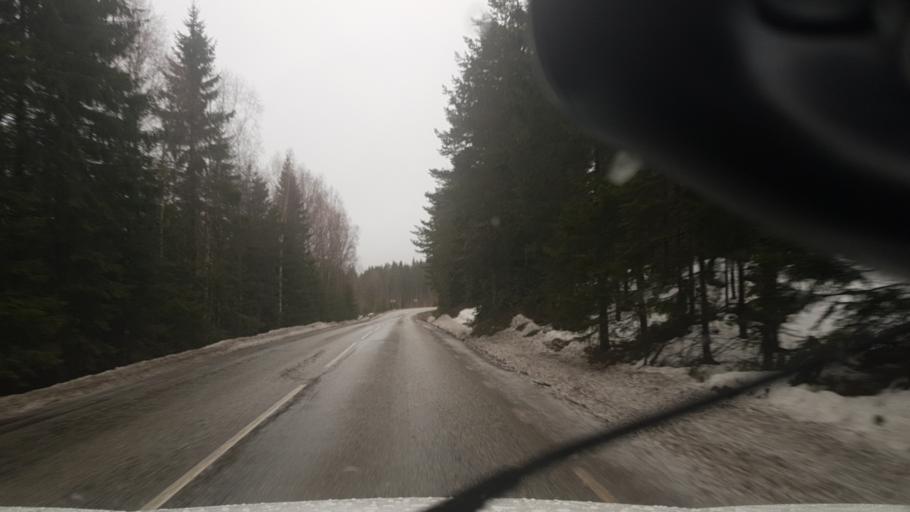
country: SE
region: Vaermland
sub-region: Eda Kommun
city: Amotfors
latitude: 59.5852
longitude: 12.2920
